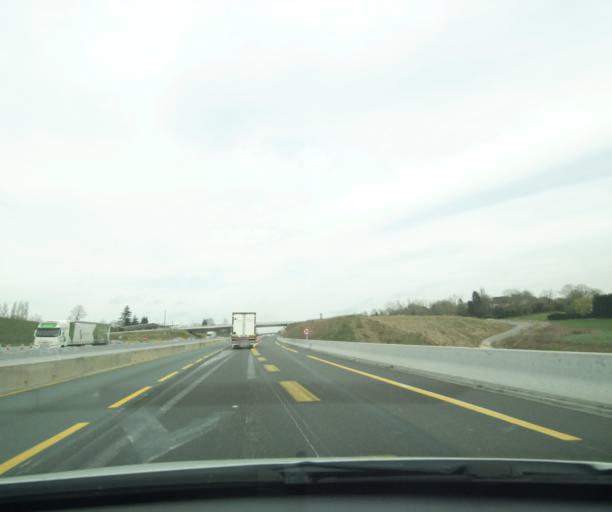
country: FR
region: Aquitaine
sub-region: Departement des Pyrenees-Atlantiques
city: Ciboure
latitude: 43.3704
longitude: -1.6798
